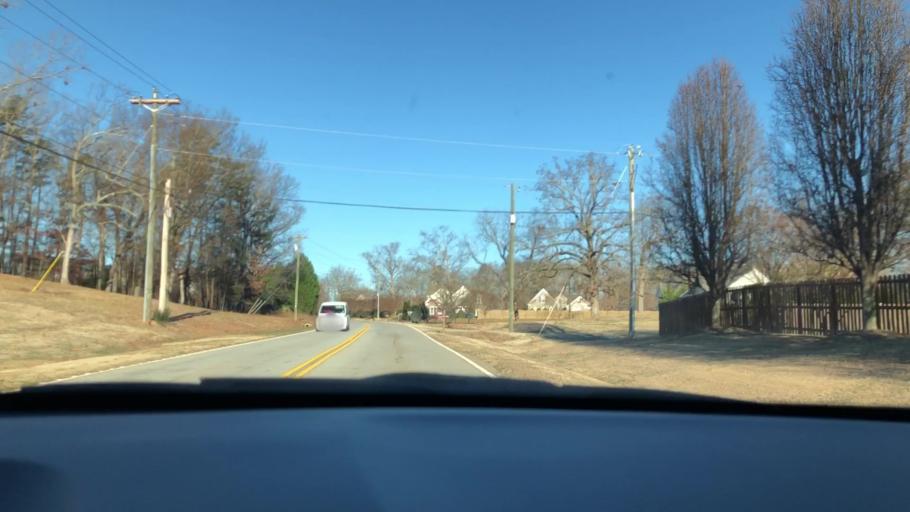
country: US
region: South Carolina
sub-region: Greenville County
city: Five Forks
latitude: 34.8273
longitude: -82.2179
